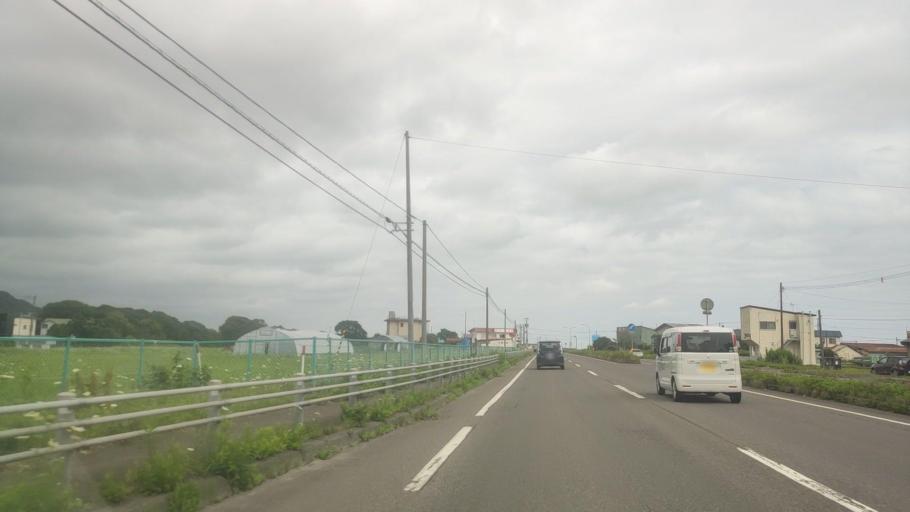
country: JP
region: Hokkaido
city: Shiraoi
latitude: 42.4635
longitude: 141.2175
